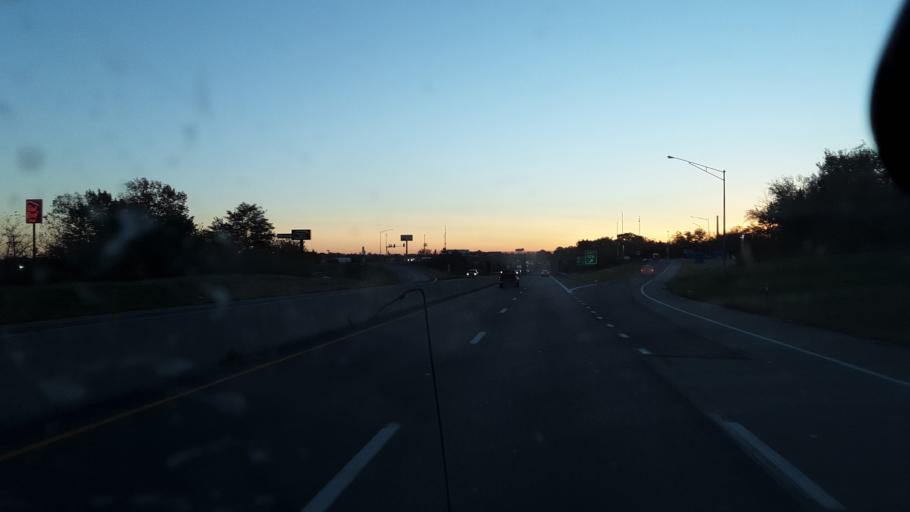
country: US
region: Missouri
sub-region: Boone County
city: Columbia
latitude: 38.9691
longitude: -92.3371
